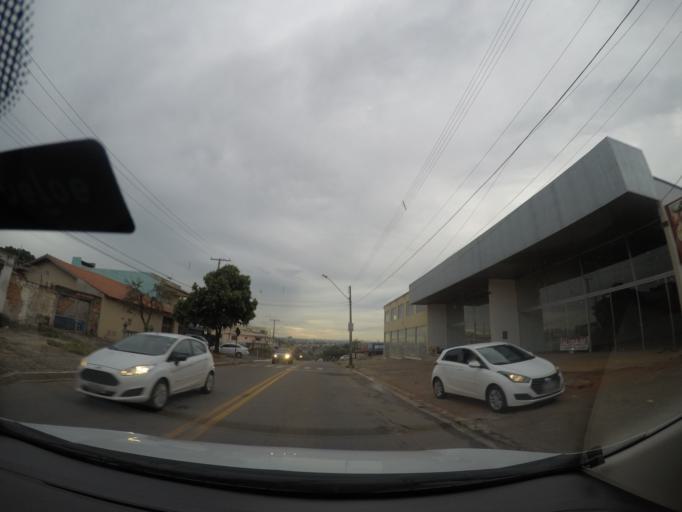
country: BR
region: Goias
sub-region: Goiania
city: Goiania
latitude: -16.6492
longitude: -49.2972
